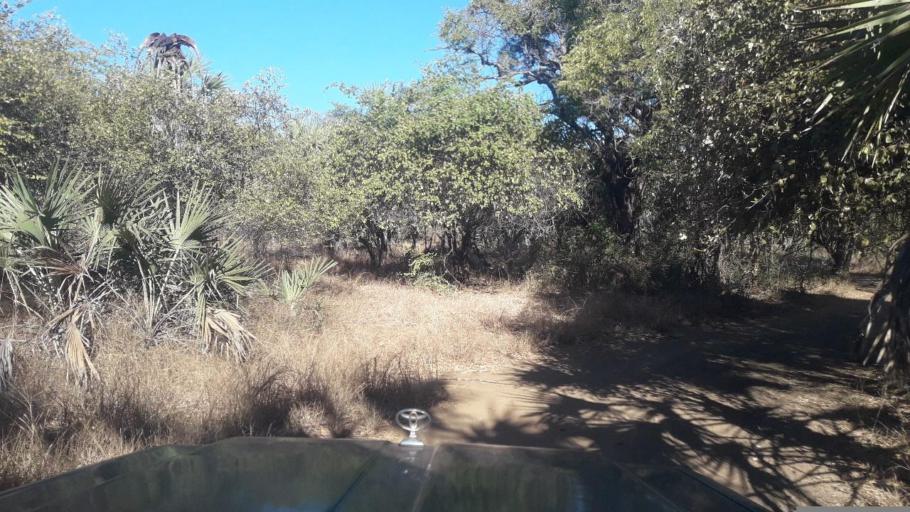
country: MG
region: Boeny
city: Sitampiky
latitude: -16.4000
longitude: 45.5979
